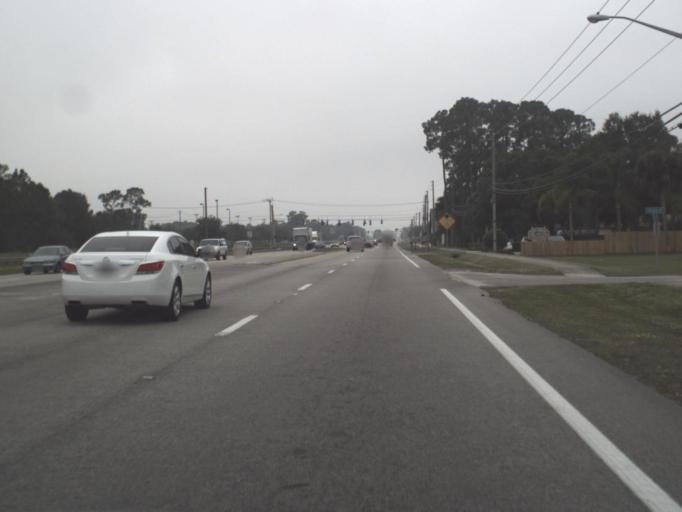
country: US
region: Florida
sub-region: Brevard County
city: June Park
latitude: 28.0415
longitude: -80.6715
